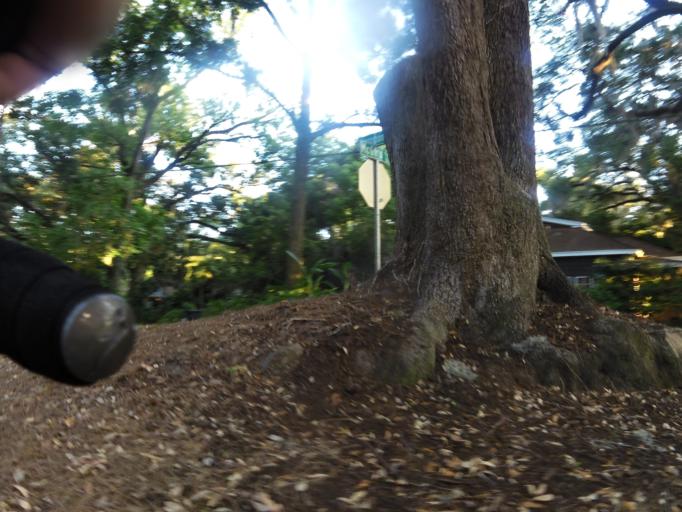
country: US
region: Florida
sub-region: Duval County
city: Jacksonville
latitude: 30.2729
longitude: -81.7126
